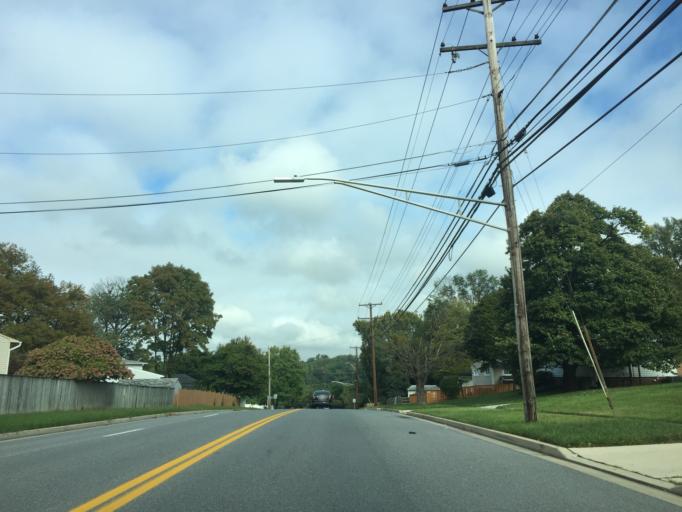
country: US
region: Maryland
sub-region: Baltimore County
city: Pikesville
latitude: 39.3782
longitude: -76.6839
